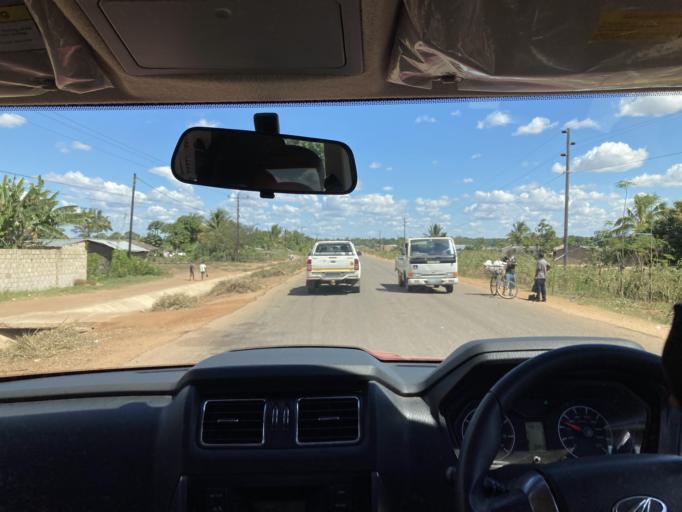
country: MZ
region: Cabo Delgado
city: Montepuez
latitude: -13.1348
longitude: 38.9907
